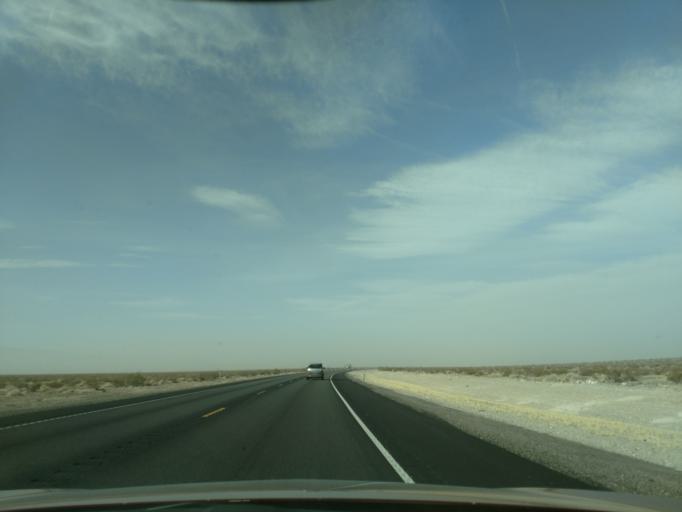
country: US
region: Nevada
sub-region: Nye County
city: Beatty
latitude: 36.6318
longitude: -116.3497
